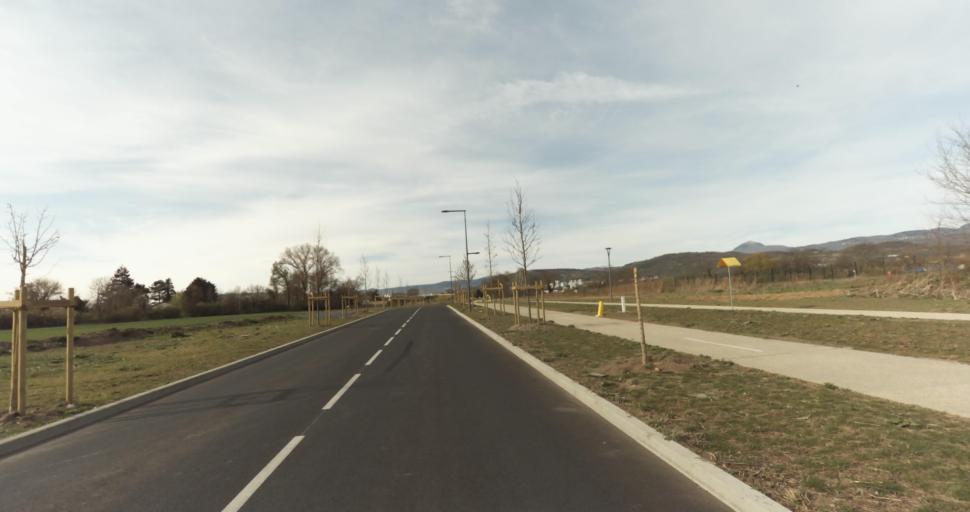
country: FR
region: Auvergne
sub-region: Departement du Puy-de-Dome
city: Gerzat
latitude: 45.8300
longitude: 3.1262
